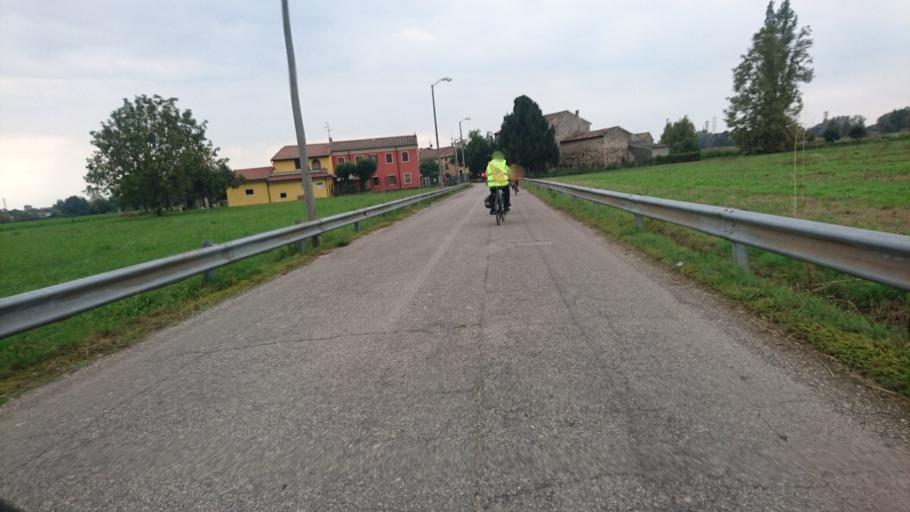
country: IT
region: Veneto
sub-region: Provincia di Verona
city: San Giovanni Lupatoto
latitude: 45.4089
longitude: 11.0579
